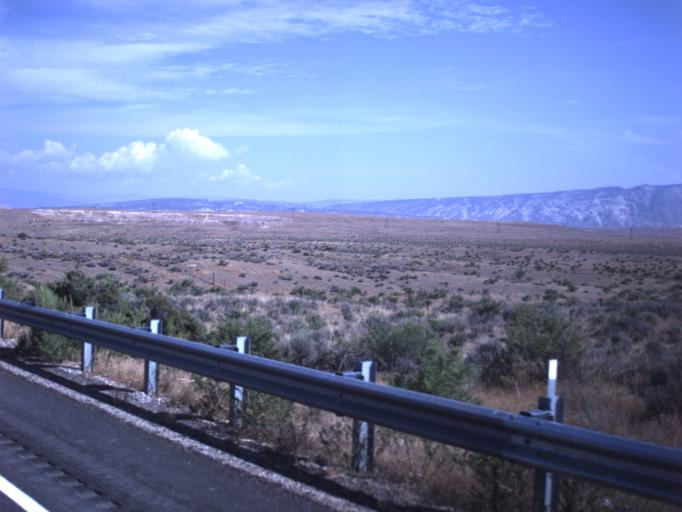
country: US
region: Utah
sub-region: Uintah County
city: Naples
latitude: 40.3544
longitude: -109.3111
